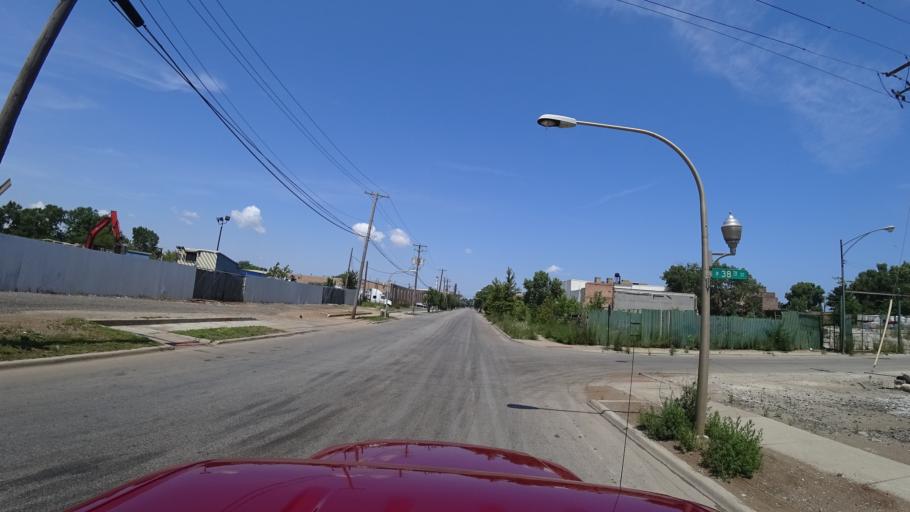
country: US
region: Illinois
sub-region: Cook County
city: Chicago
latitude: 41.8250
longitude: -87.6556
